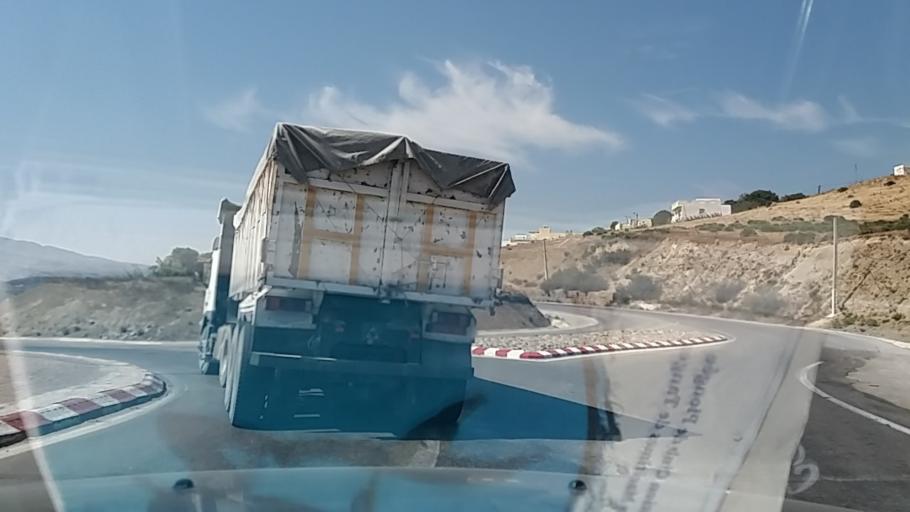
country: MA
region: Tanger-Tetouan
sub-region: Tetouan
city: Saddina
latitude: 35.5582
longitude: -5.4539
